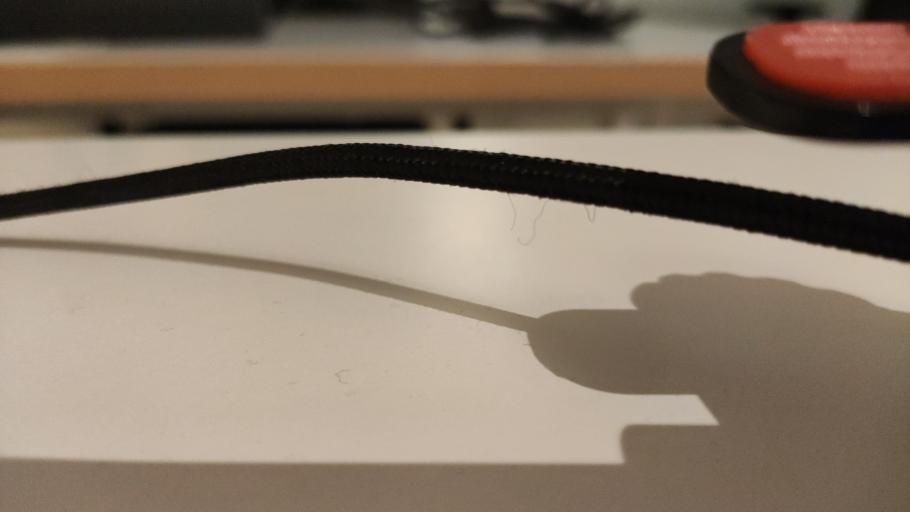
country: RU
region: Moskovskaya
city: Novoye
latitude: 55.6425
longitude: 38.9291
